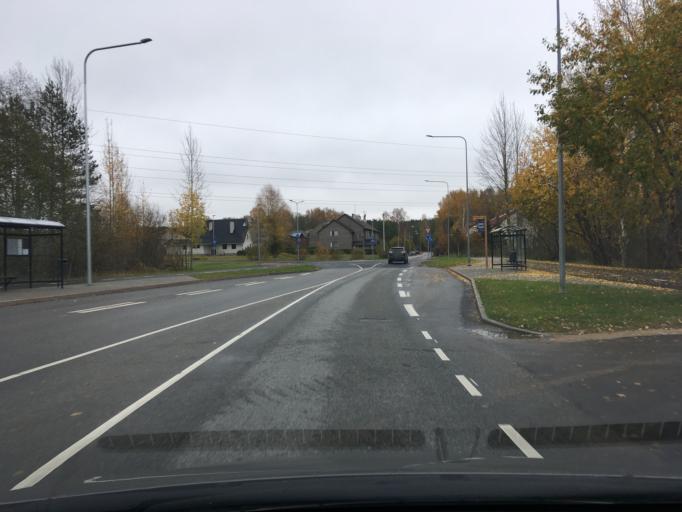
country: EE
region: Tartu
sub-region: Tartu linn
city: Tartu
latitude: 58.3597
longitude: 26.7776
